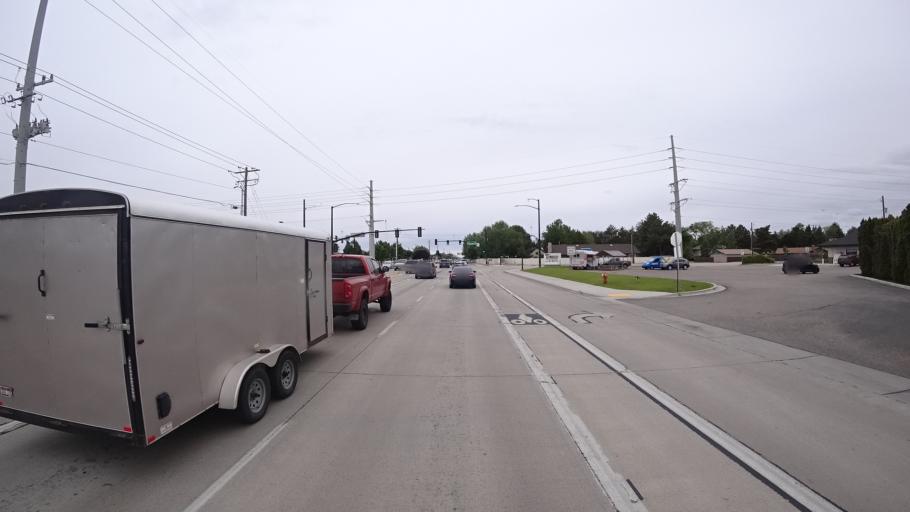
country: US
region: Idaho
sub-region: Ada County
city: Meridian
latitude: 43.6339
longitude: -116.3336
